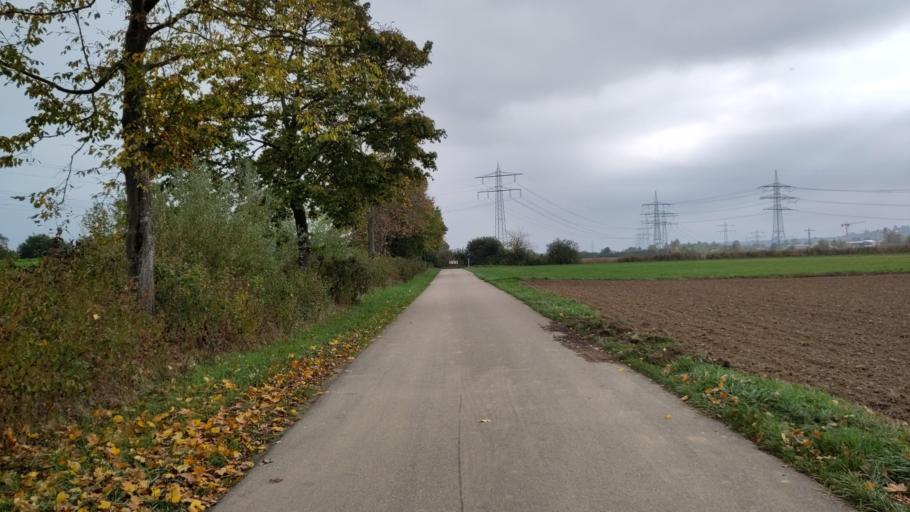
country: DE
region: Baden-Wuerttemberg
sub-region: Freiburg Region
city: Riegel
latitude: 48.1328
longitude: 7.7571
